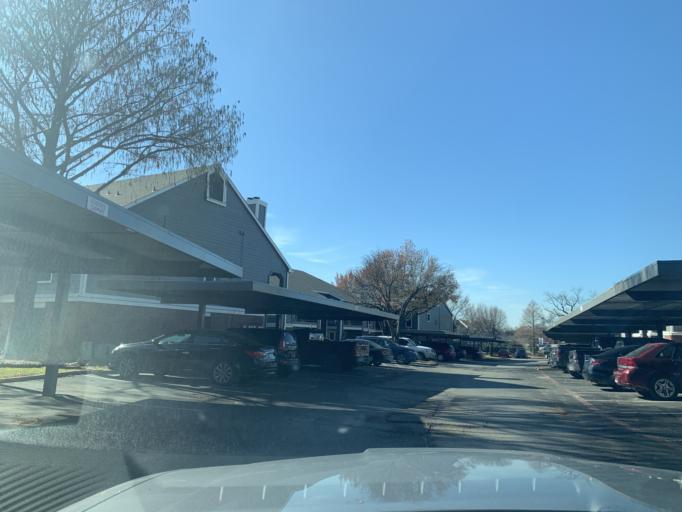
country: US
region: Texas
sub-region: Tarrant County
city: Bedford
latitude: 32.8437
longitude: -97.1408
